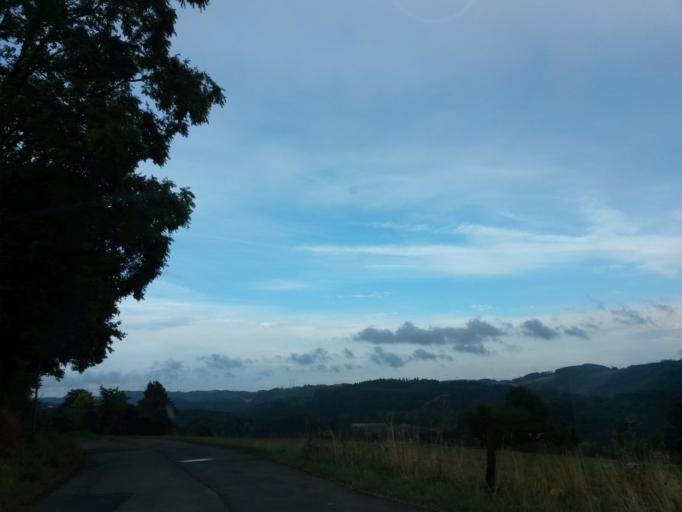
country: DE
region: North Rhine-Westphalia
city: Bergneustadt
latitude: 51.0446
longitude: 7.6171
